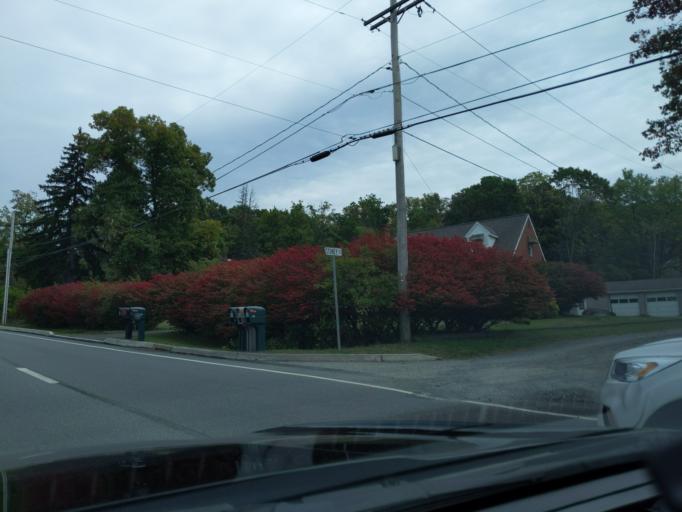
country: US
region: Pennsylvania
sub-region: Blair County
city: Lakemont
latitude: 40.4778
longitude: -78.3901
